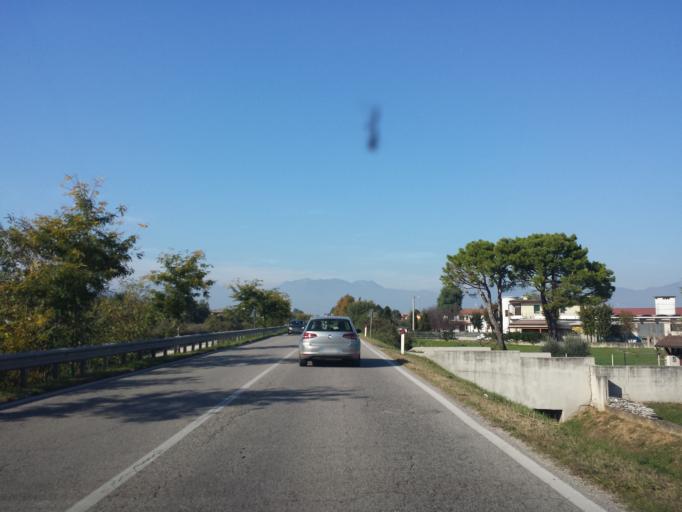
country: IT
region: Veneto
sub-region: Provincia di Vicenza
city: Castelnovo
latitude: 45.6109
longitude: 11.4702
